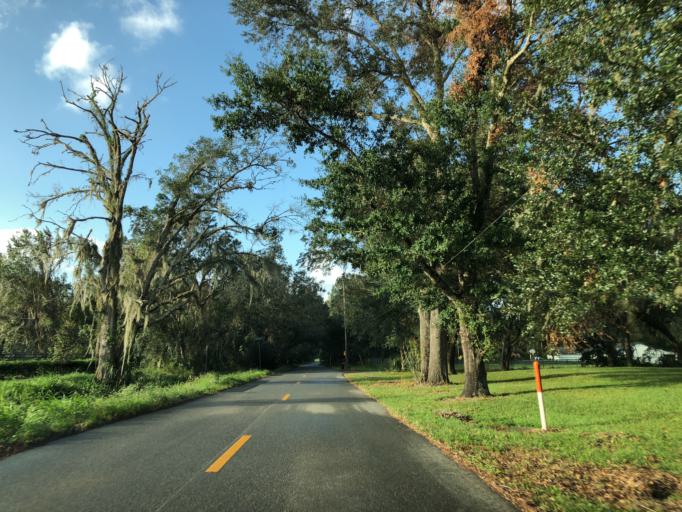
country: US
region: Florida
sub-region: Seminole County
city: Oviedo
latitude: 28.6842
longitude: -81.1798
